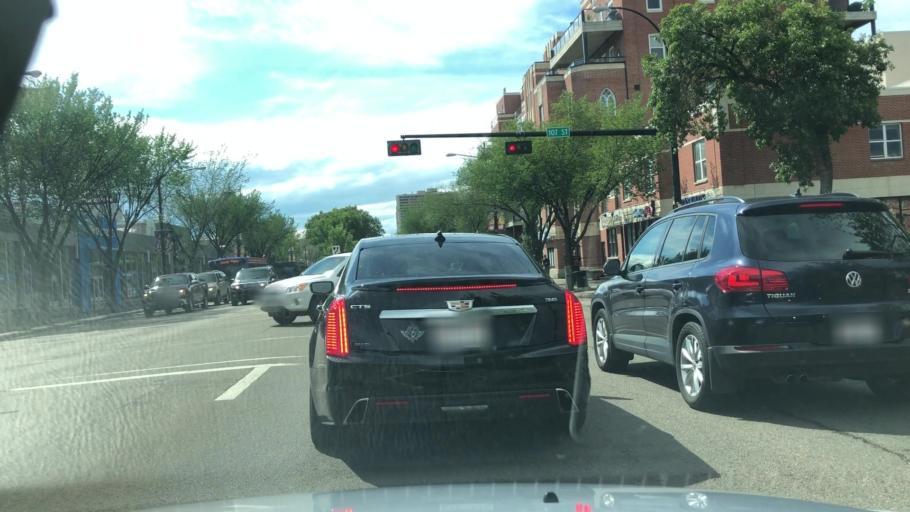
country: CA
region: Alberta
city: Edmonton
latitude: 53.5181
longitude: -113.5059
